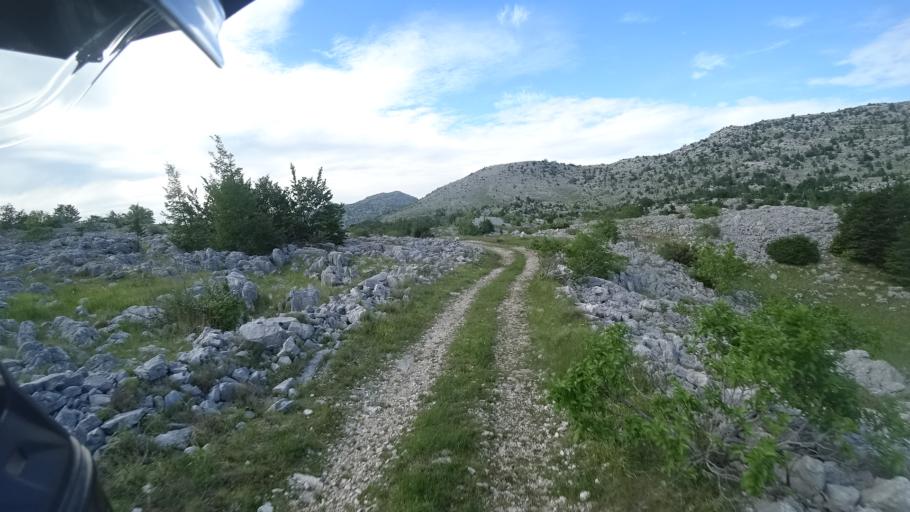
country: HR
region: Splitsko-Dalmatinska
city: Hrvace
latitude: 43.8070
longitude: 16.4336
